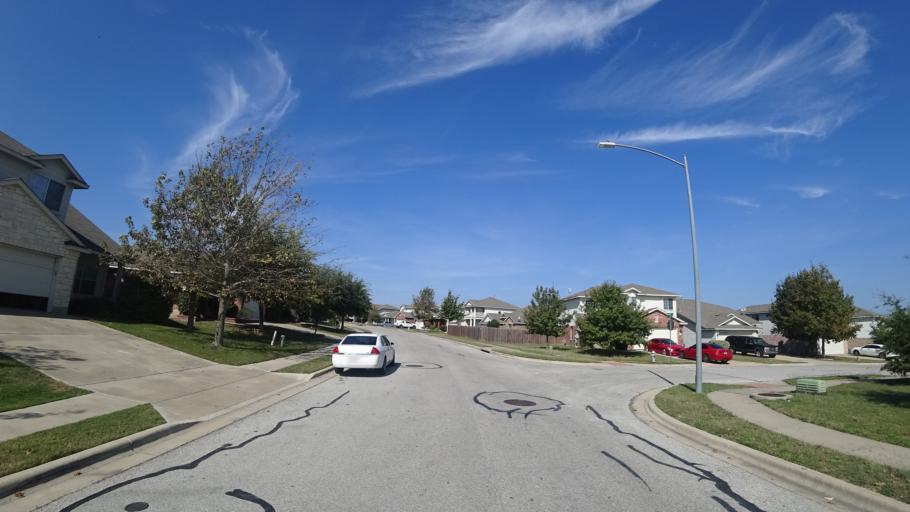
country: US
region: Texas
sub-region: Travis County
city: Pflugerville
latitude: 30.4266
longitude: -97.6376
